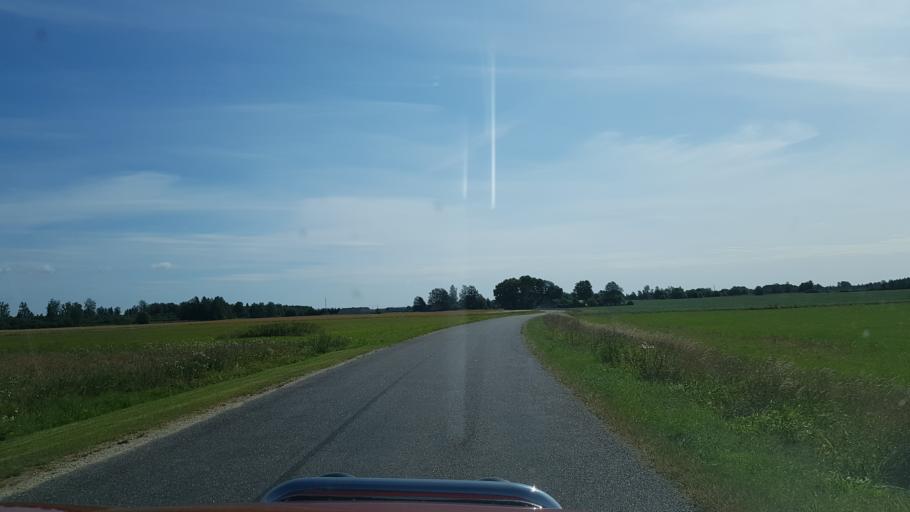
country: EE
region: Jaervamaa
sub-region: Jaerva-Jaani vald
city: Jarva-Jaani
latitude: 59.1152
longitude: 25.7394
